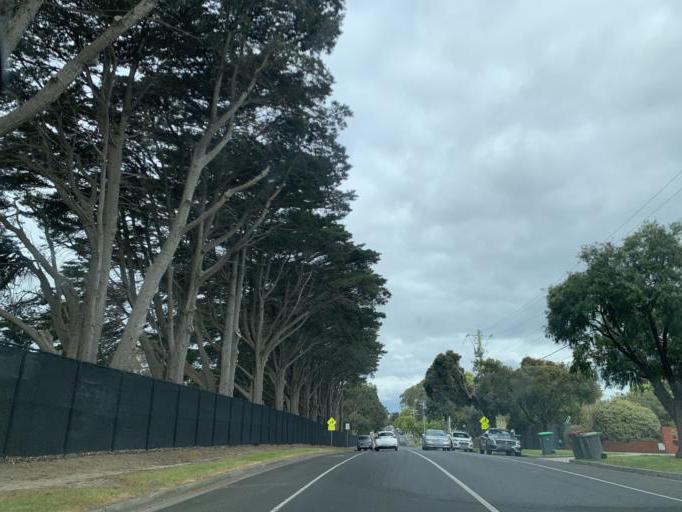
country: AU
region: Victoria
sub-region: Bayside
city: Cheltenham
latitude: -37.9705
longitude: 145.0384
